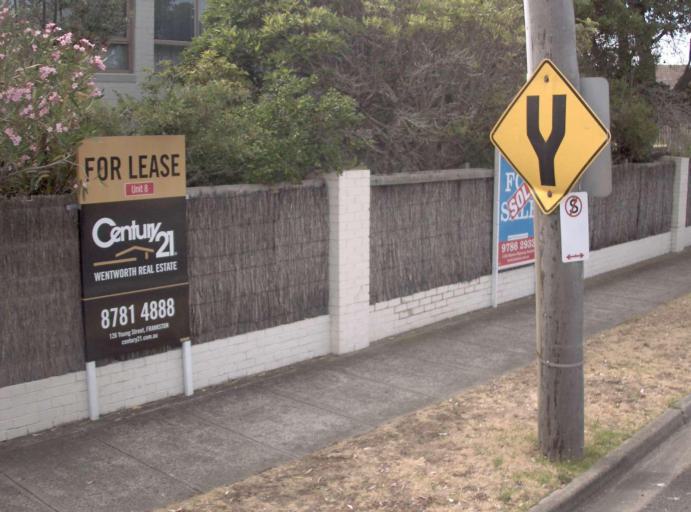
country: AU
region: Victoria
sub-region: Frankston
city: Frankston East
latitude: -38.1280
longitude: 145.1241
